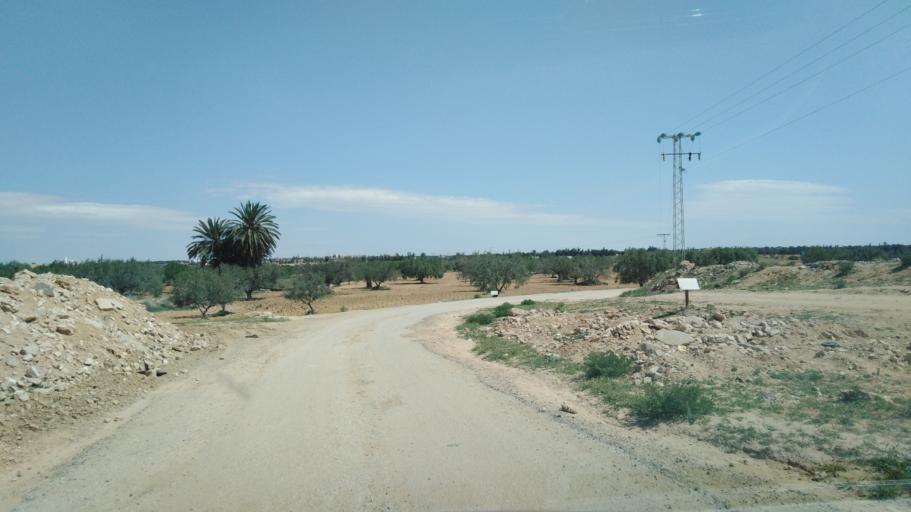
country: TN
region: Safaqis
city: Sfax
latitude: 34.7506
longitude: 10.5264
